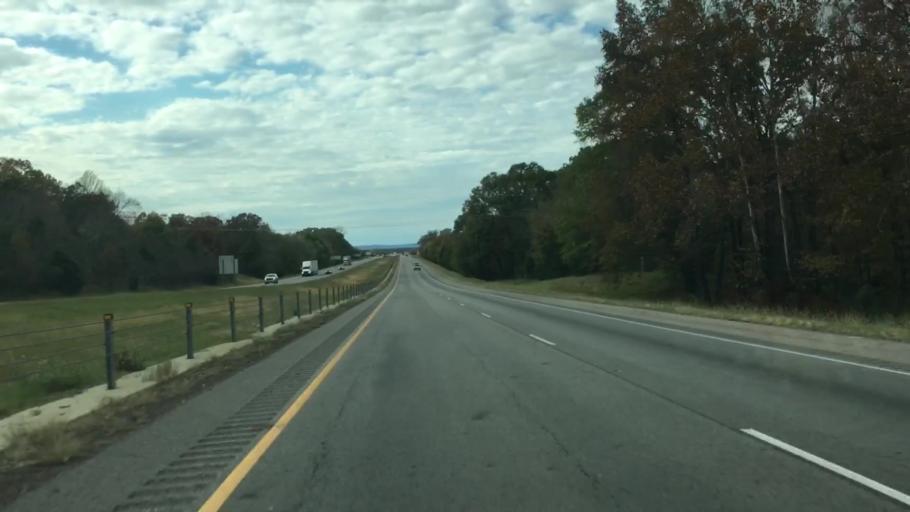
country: US
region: Arkansas
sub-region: Conway County
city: Morrilton
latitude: 35.1820
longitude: -92.7629
